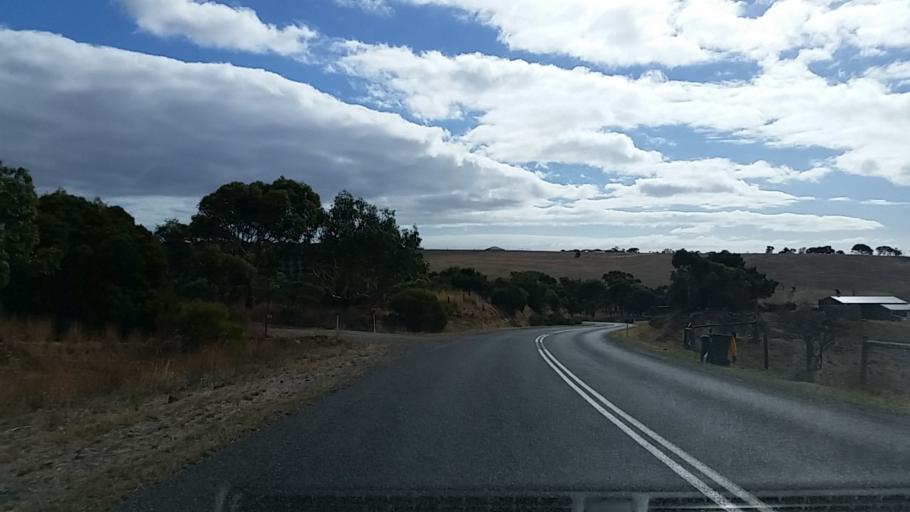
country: AU
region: South Australia
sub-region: Yankalilla
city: Normanville
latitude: -35.4139
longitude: 138.3585
